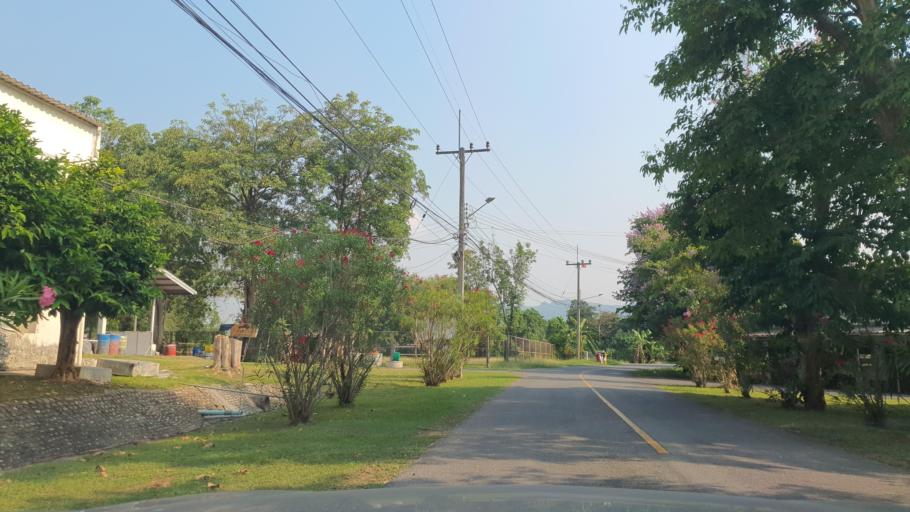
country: TH
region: Kanchanaburi
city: Sai Yok
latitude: 14.2278
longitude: 99.2349
